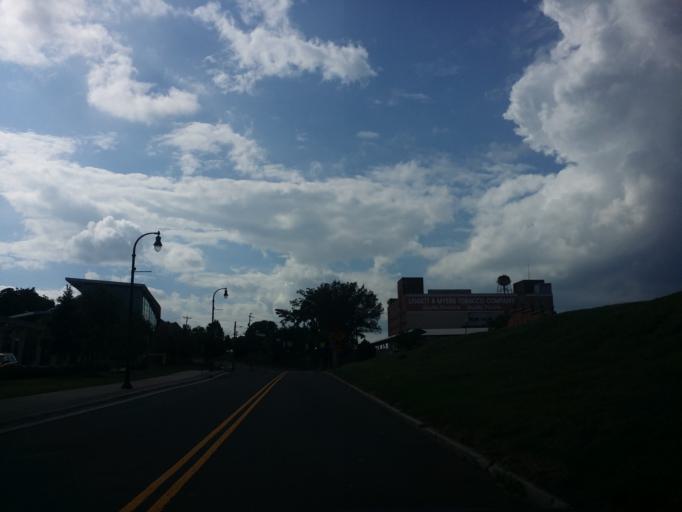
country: US
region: North Carolina
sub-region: Durham County
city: Durham
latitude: 35.9963
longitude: -78.9056
